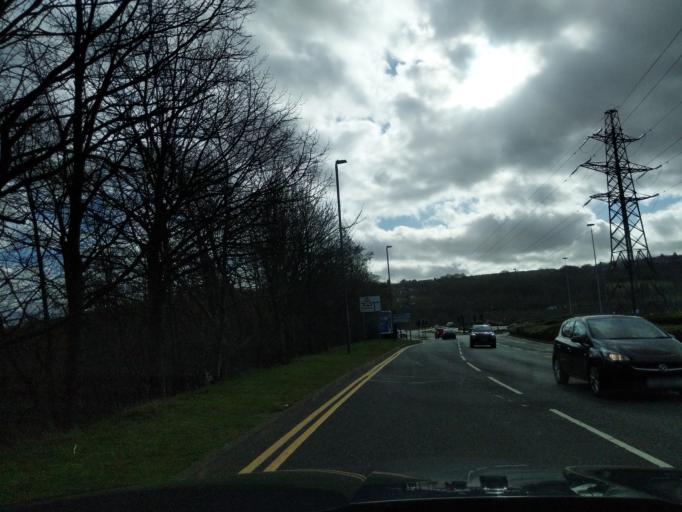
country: GB
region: England
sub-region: Newcastle upon Tyne
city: Benwell
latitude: 54.9573
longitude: -1.6624
